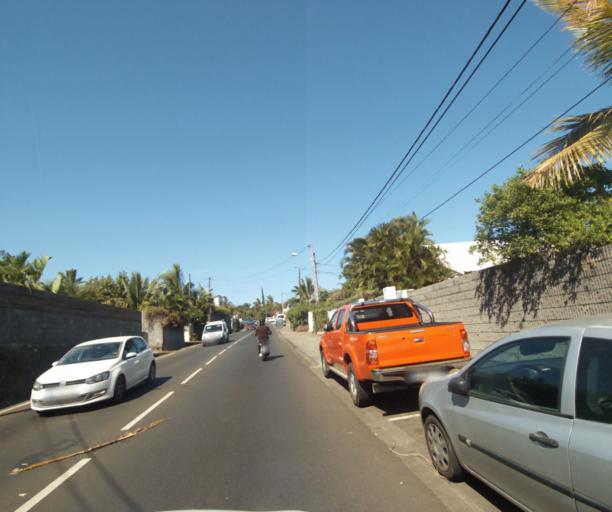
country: RE
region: Reunion
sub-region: Reunion
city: La Possession
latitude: -20.9856
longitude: 55.3335
